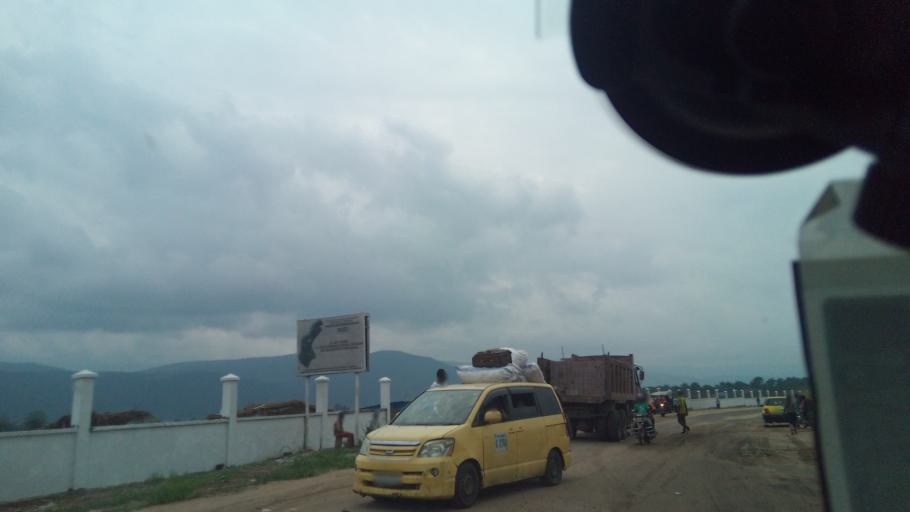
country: CG
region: Brazzaville
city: Brazzaville
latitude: -4.0796
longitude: 15.5413
